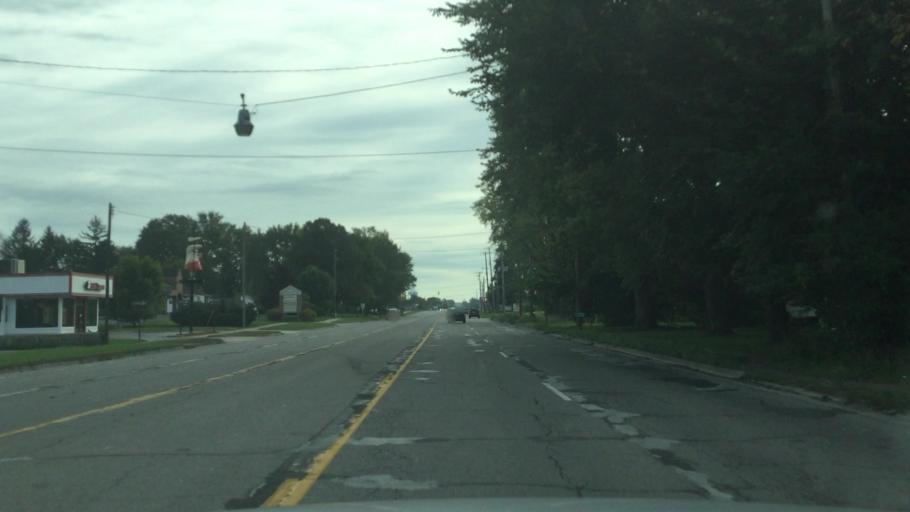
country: US
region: Michigan
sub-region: Genesee County
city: Flint
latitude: 42.9740
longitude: -83.6912
